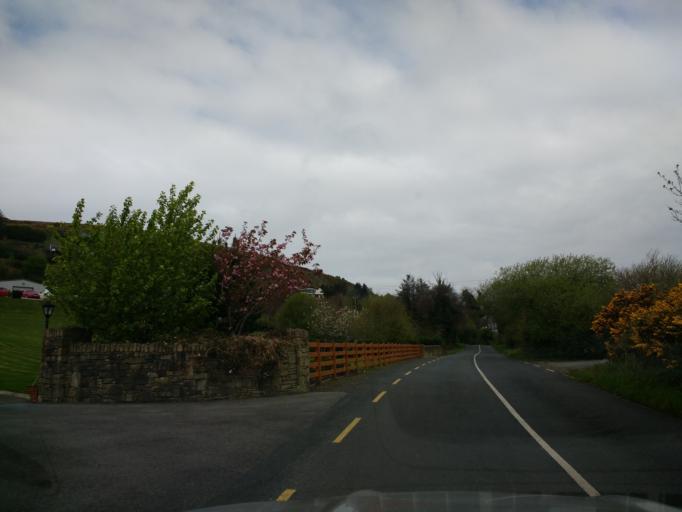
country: IE
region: Ulster
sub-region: County Donegal
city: Buncrana
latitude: 55.1457
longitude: -7.5459
